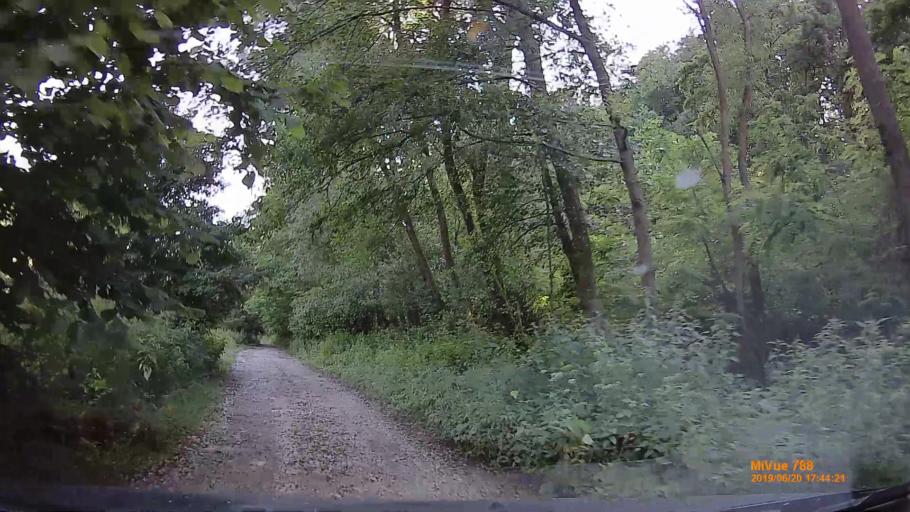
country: HU
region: Baranya
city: Buekkoesd
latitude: 46.1365
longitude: 18.0033
